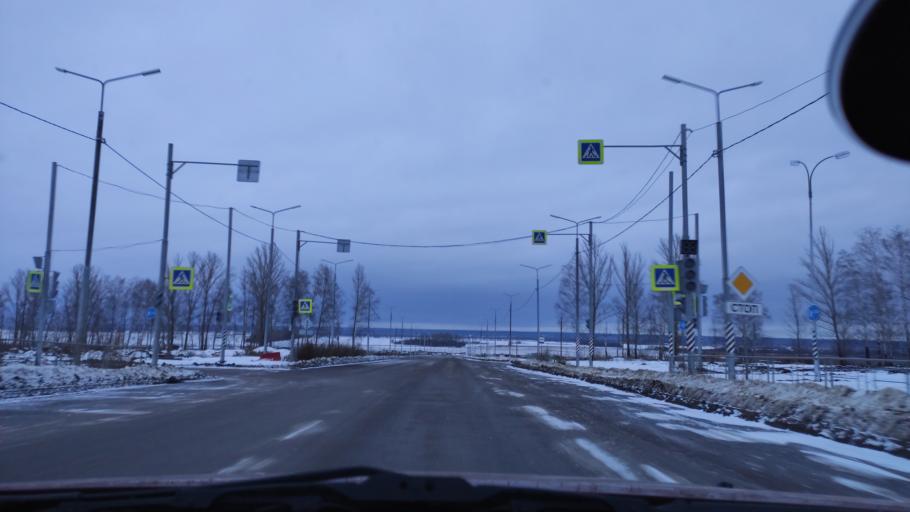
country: RU
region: Tambov
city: Tambov
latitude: 52.7803
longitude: 41.4208
